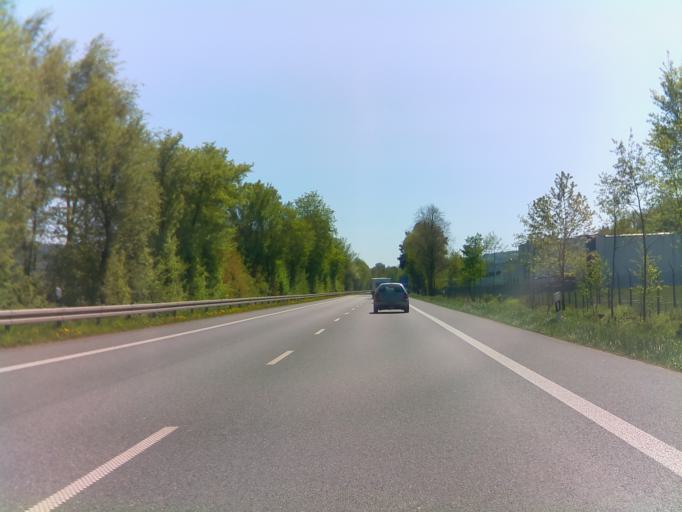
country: DE
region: Hesse
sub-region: Regierungsbezirk Kassel
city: Niederaula
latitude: 50.7854
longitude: 9.5928
